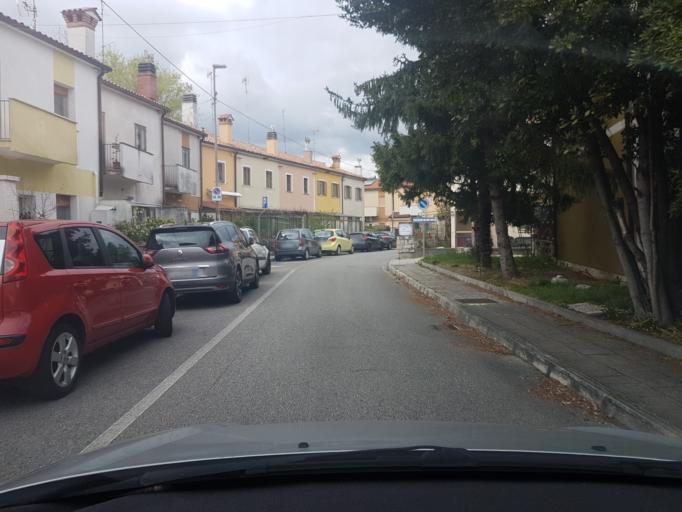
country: IT
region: Friuli Venezia Giulia
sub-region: Provincia di Trieste
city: Duino
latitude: 45.7811
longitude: 13.5876
